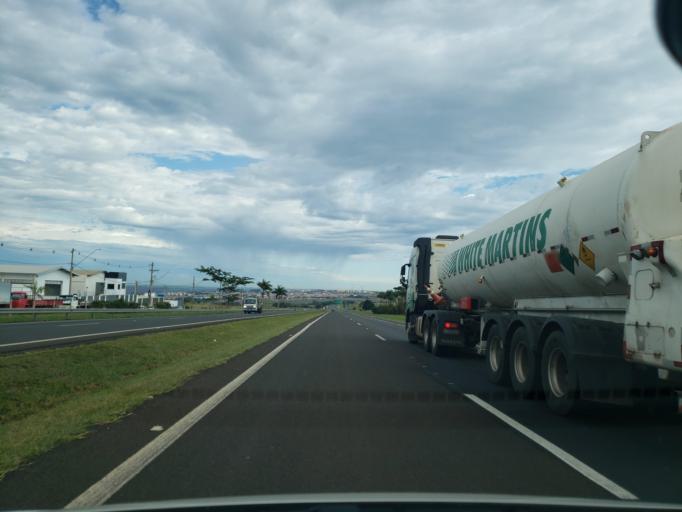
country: BR
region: Sao Paulo
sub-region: Jau
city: Jau
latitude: -22.2662
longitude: -48.5101
